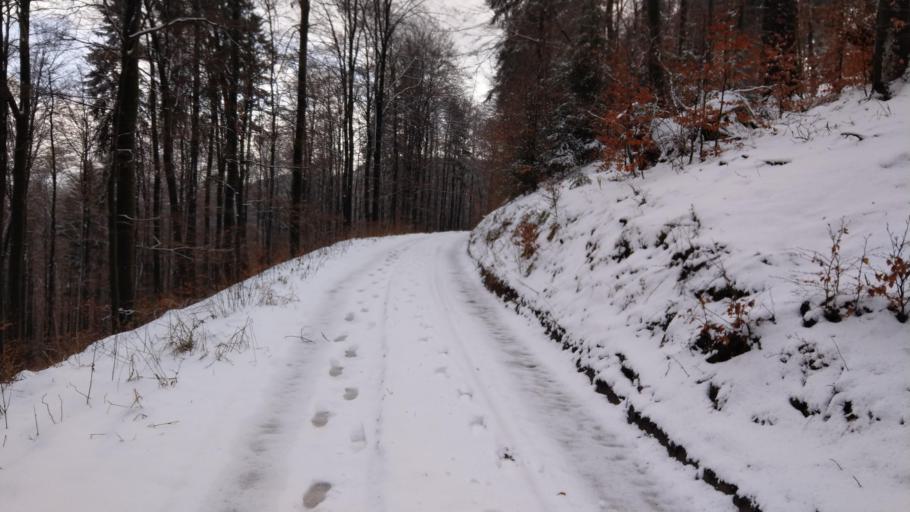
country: DE
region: Hesse
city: Willingen
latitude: 51.3171
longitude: 8.5826
